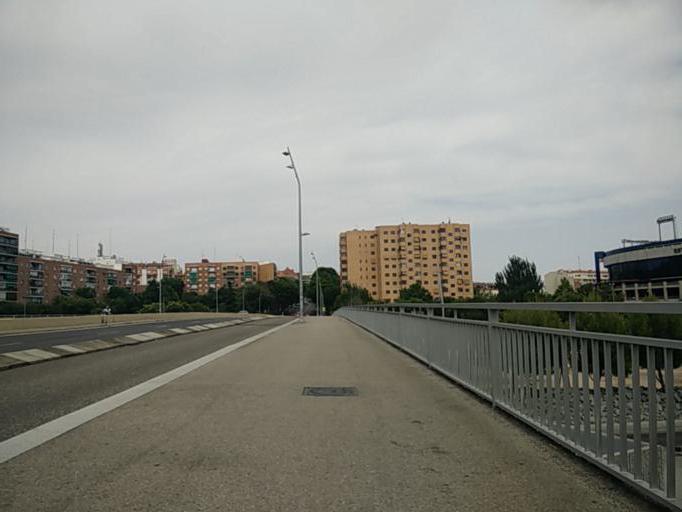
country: ES
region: Madrid
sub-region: Provincia de Madrid
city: Carabanchel
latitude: 40.4036
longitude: -3.7236
